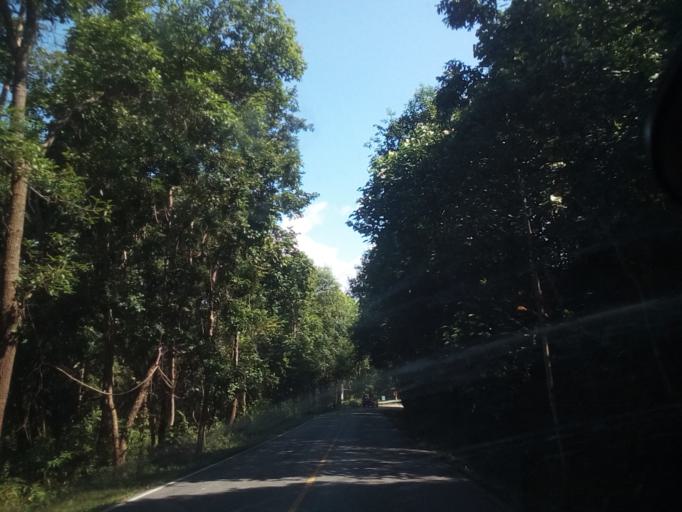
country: TH
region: Chiang Mai
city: Samoeng
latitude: 18.8586
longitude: 98.6721
